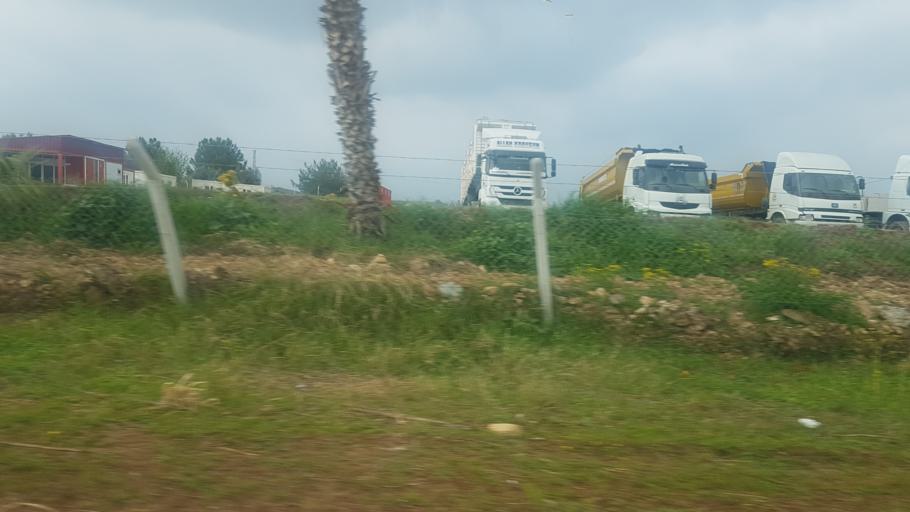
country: TR
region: Adana
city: Seyhan
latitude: 37.0541
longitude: 35.2161
